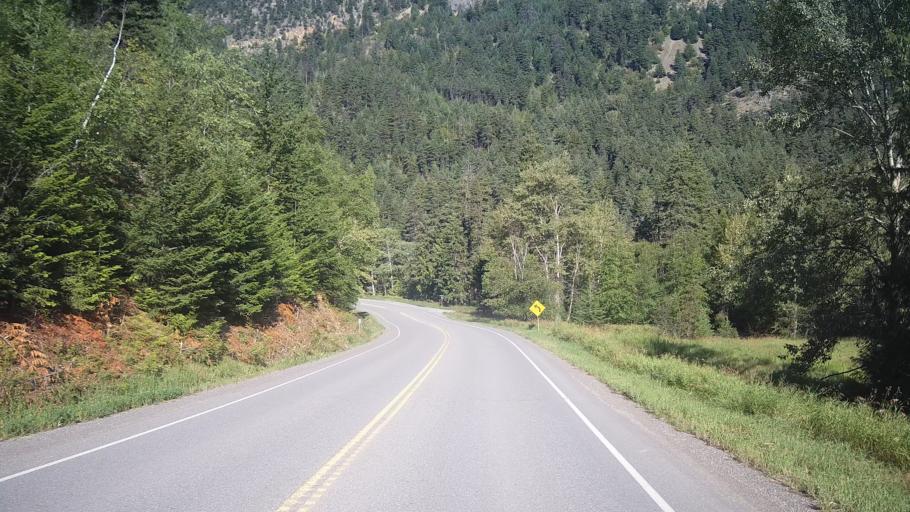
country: CA
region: British Columbia
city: Lillooet
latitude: 50.6387
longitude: -122.0852
